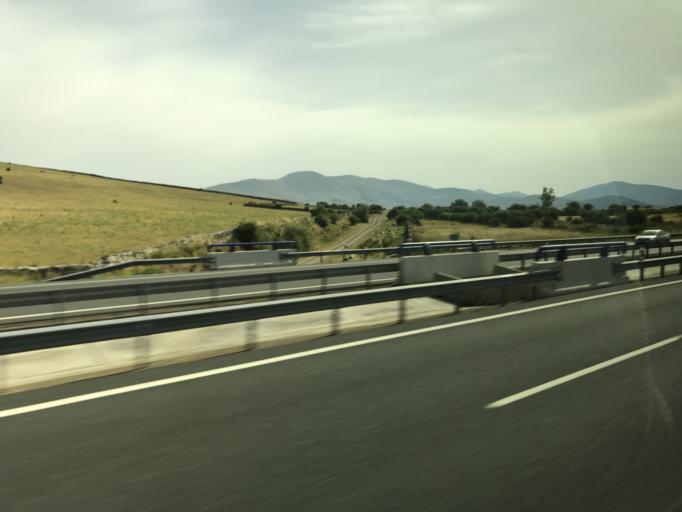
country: ES
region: Castille and Leon
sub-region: Provincia de Segovia
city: Vegas de Matute
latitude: 40.7394
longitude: -4.2403
